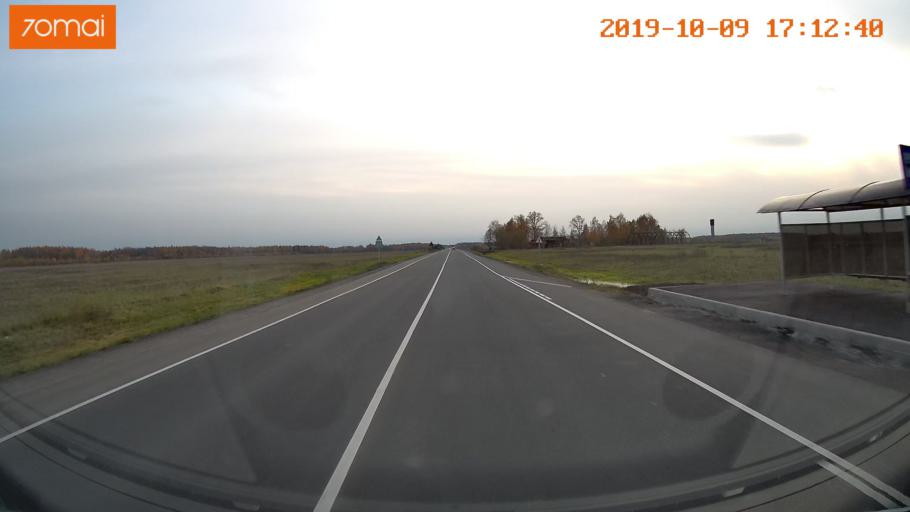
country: RU
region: Ivanovo
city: Privolzhsk
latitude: 57.3257
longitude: 41.2382
